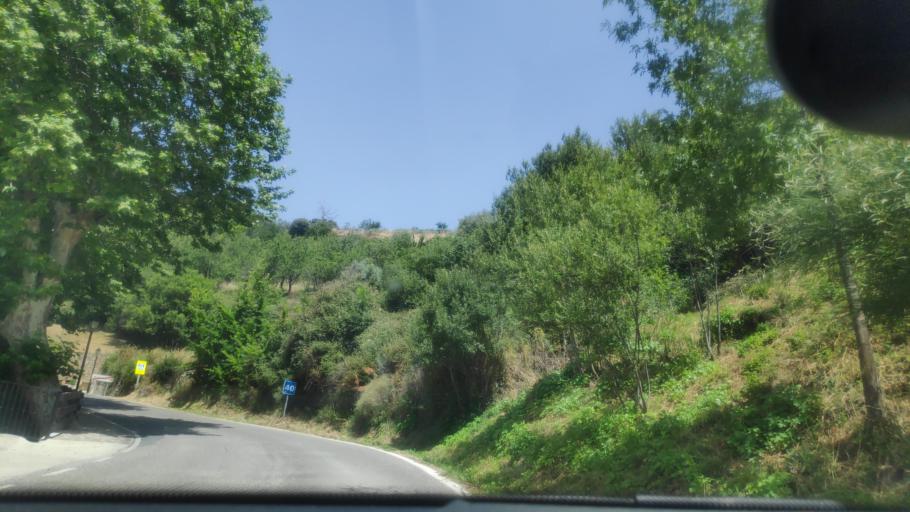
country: ES
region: Andalusia
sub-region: Provincia de Granada
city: Busquistar
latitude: 36.9389
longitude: -3.2954
